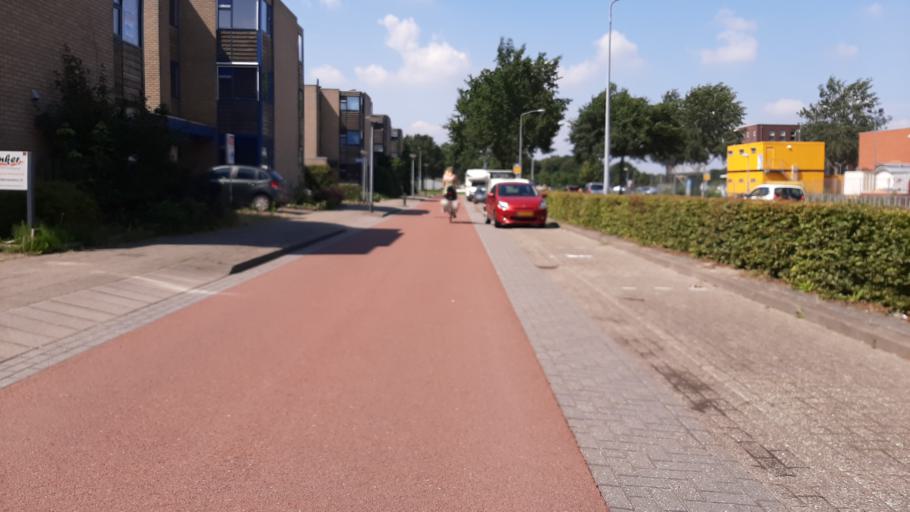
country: NL
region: Flevoland
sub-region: Gemeente Zeewolde
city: Zeewolde
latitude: 52.3295
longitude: 5.5407
